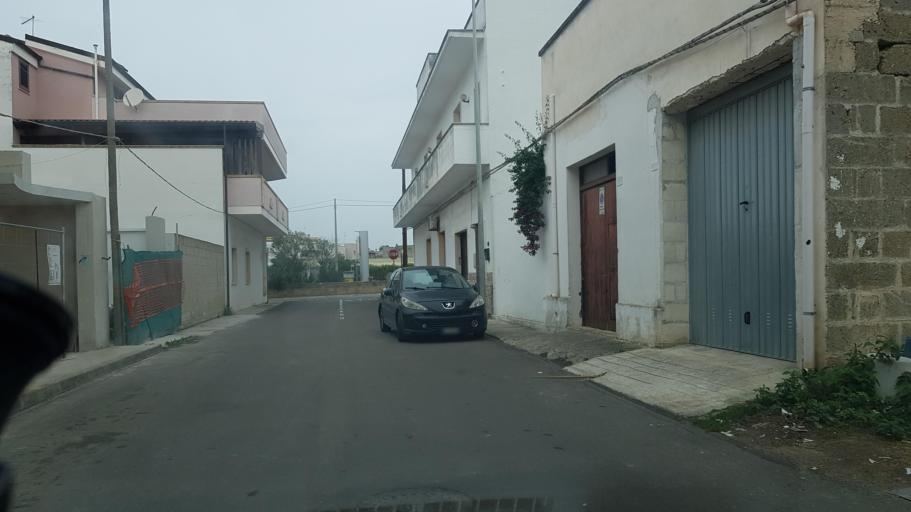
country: IT
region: Apulia
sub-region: Provincia di Lecce
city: Leverano
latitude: 40.2881
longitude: 18.0060
